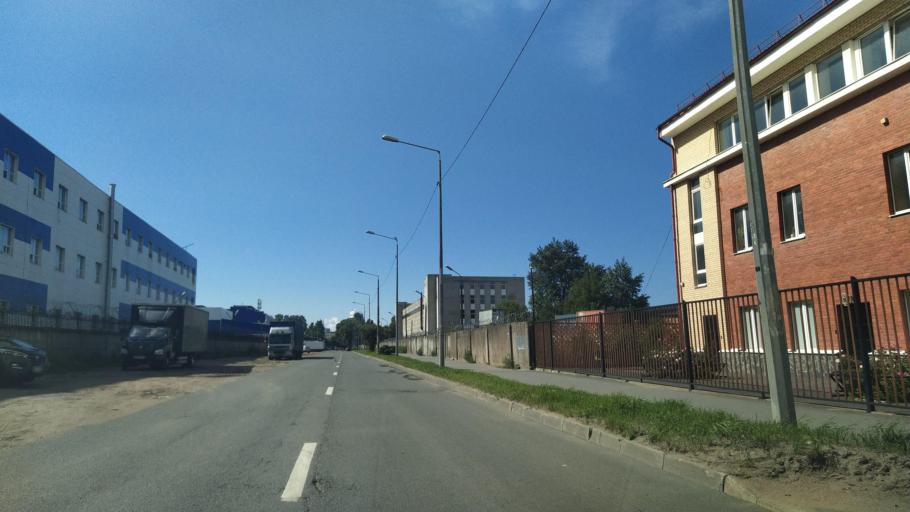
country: RU
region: Leningrad
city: Finlyandskiy
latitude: 59.9758
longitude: 30.3599
